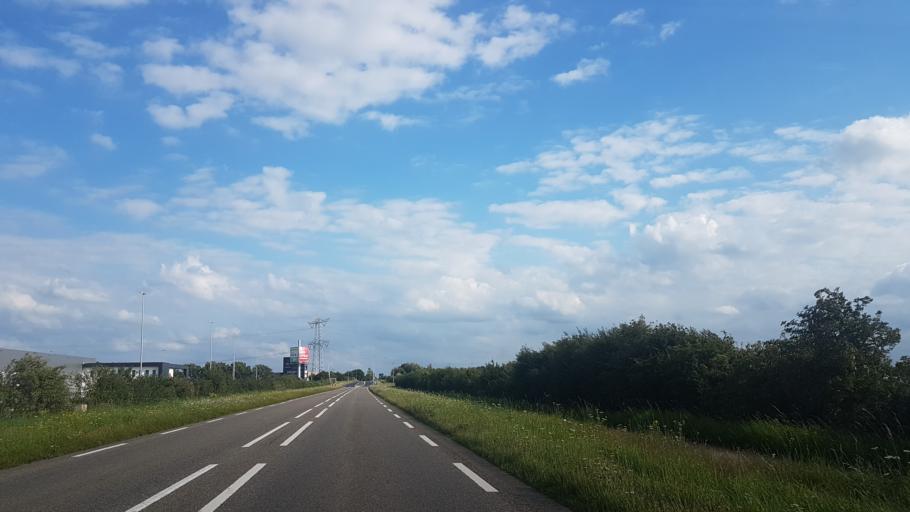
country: NL
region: North Brabant
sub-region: Gemeente Made en Drimmelen
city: Made
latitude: 51.6782
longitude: 4.8197
